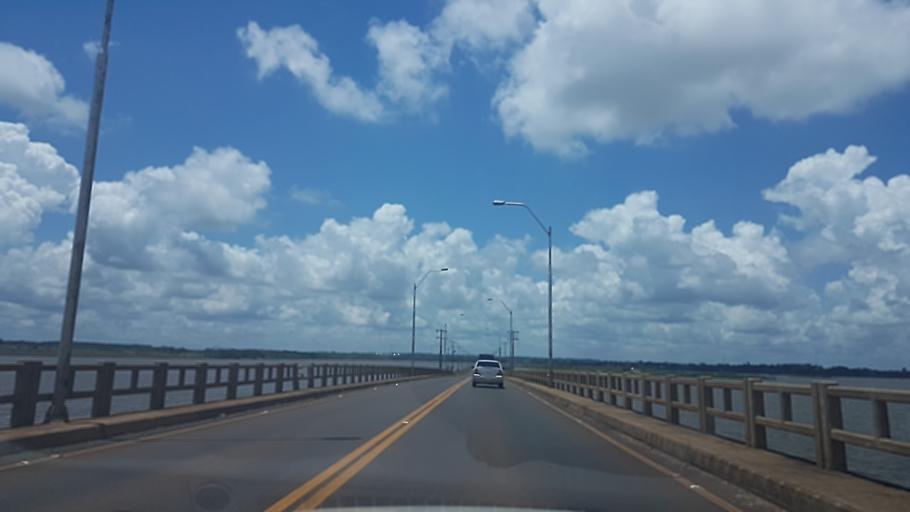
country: PY
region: Itapua
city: Carmen del Parana
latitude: -27.2052
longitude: -56.1691
